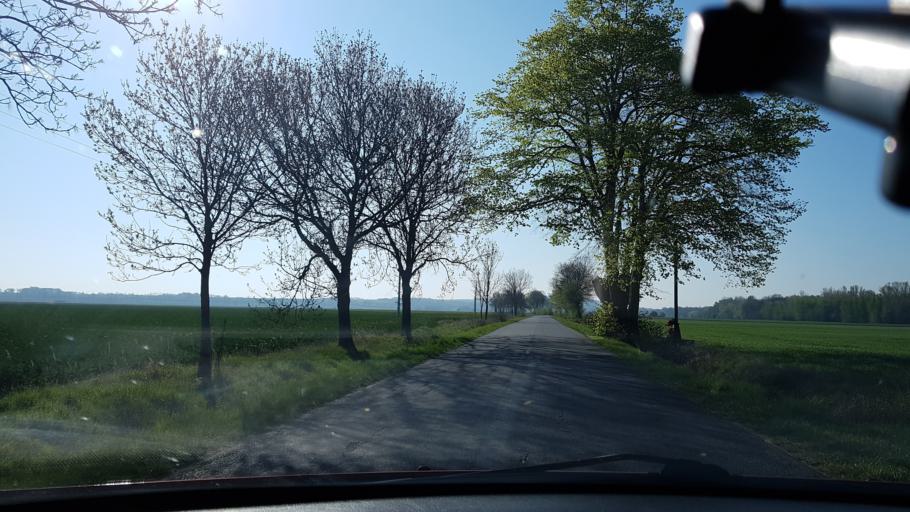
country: PL
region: Opole Voivodeship
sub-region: Powiat nyski
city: Nysa
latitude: 50.4265
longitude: 17.3095
